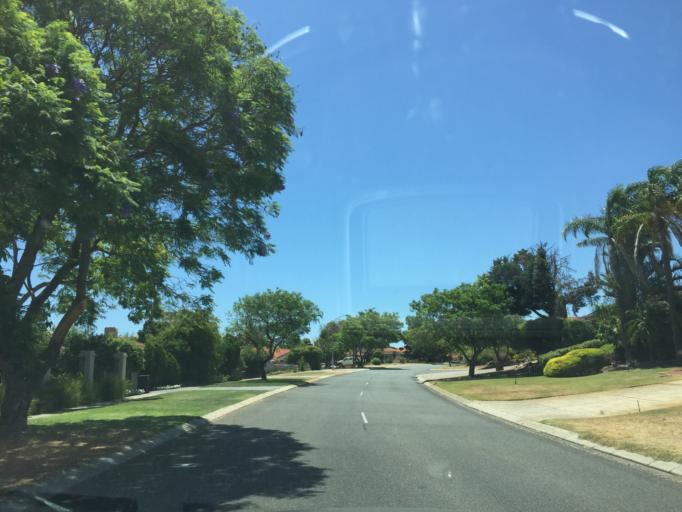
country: AU
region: Western Australia
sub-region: Melville
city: Winthrop
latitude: -32.0625
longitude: 115.8364
